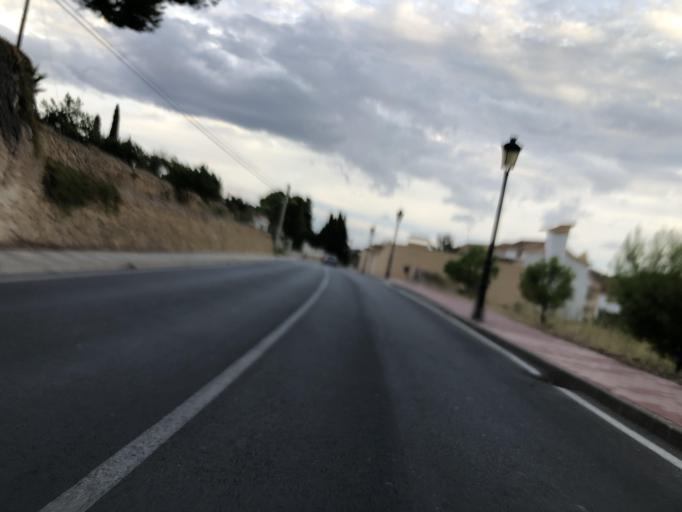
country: ES
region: Valencia
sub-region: Provincia de Alicante
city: Polop
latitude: 38.6248
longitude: -0.1351
